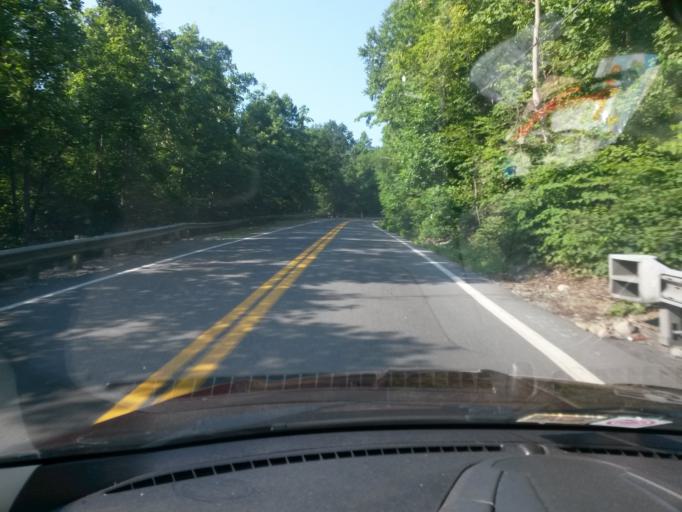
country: US
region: West Virginia
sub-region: Wyoming County
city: Pineville
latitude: 37.5580
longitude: -81.5425
